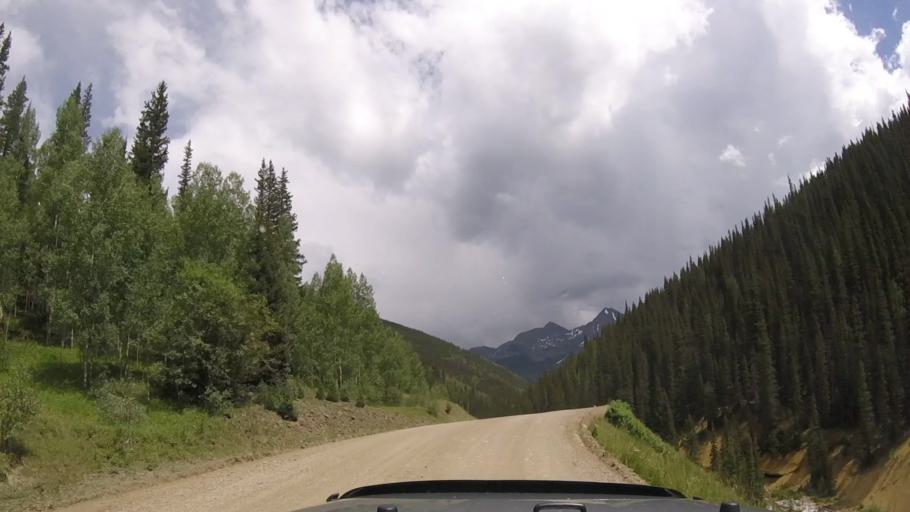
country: US
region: Colorado
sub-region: San Juan County
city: Silverton
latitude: 37.8351
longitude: -107.6769
